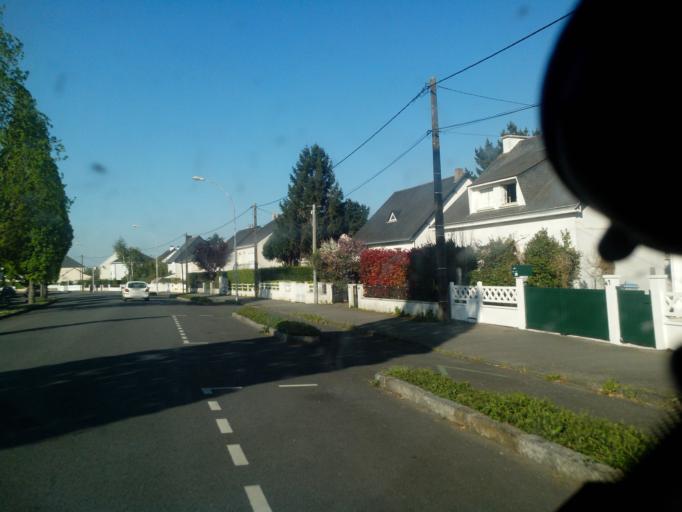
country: FR
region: Pays de la Loire
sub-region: Departement de la Loire-Atlantique
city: Orvault
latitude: 47.2516
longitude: -1.6059
